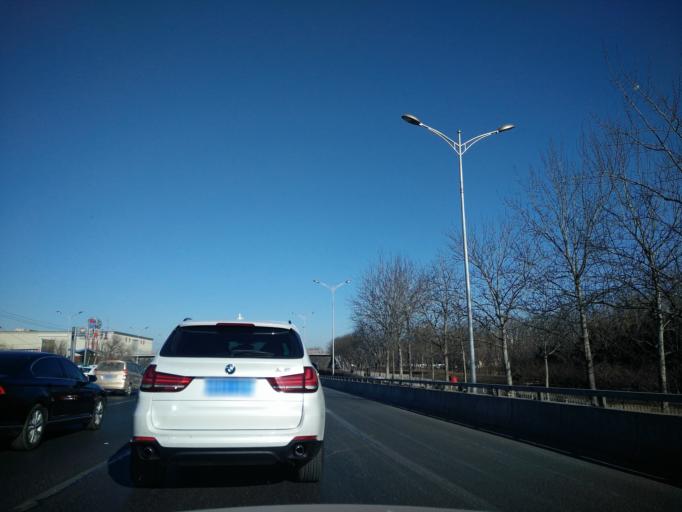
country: CN
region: Beijing
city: Huaxiang
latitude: 39.8341
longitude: 116.3399
